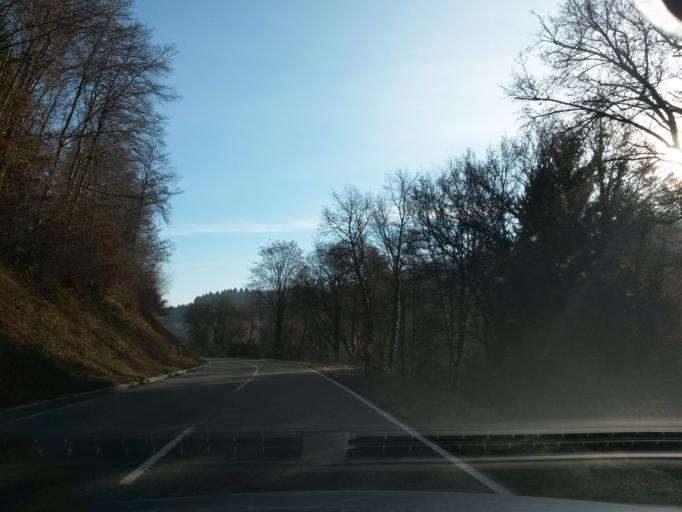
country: DE
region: Baden-Wuerttemberg
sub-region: Karlsruhe Region
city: Ispringen
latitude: 48.9240
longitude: 8.6559
